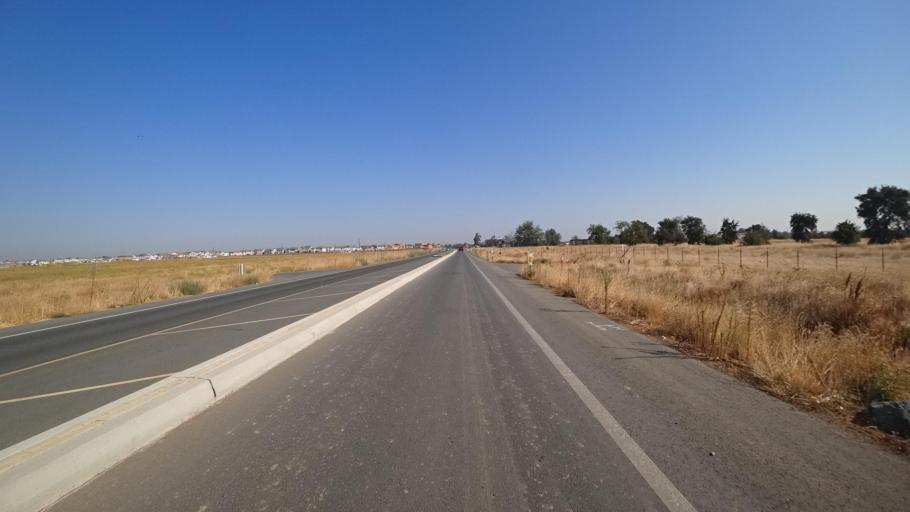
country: US
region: California
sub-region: Sacramento County
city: Elk Grove
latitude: 38.3875
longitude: -121.3992
